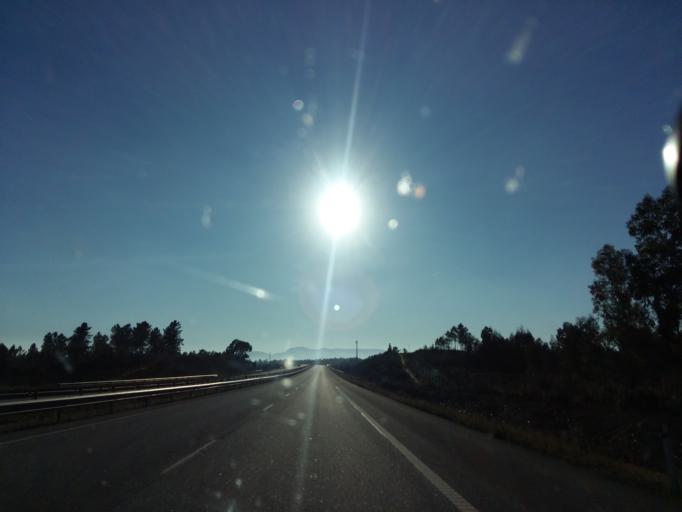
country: PT
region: Castelo Branco
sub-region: Castelo Branco
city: Castelo Branco
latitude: 39.7489
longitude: -7.6299
